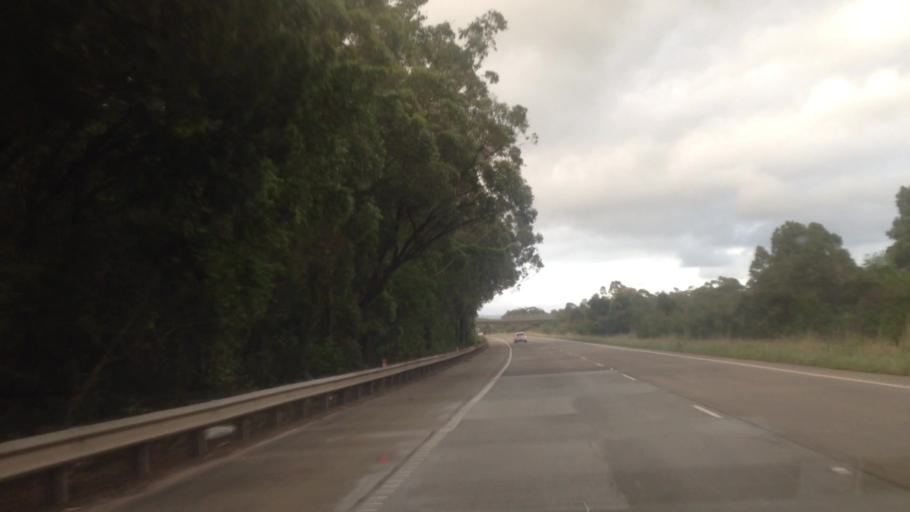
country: AU
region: New South Wales
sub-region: Wyong Shire
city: Charmhaven
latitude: -33.1860
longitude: 151.4676
